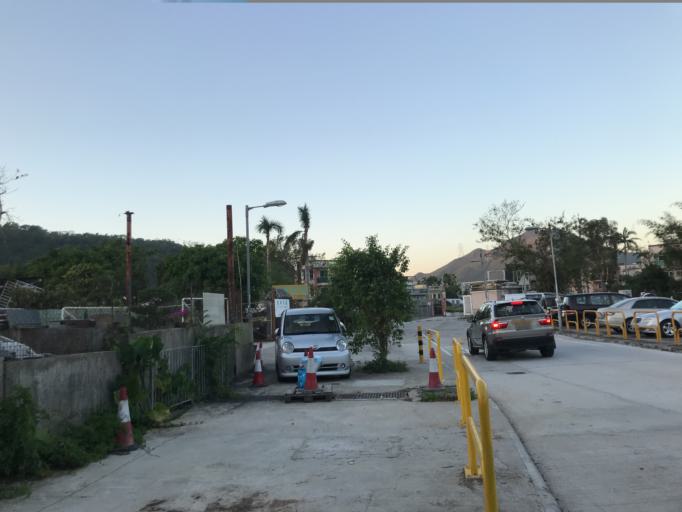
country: HK
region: Tai Po
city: Tai Po
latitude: 22.4677
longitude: 114.1502
